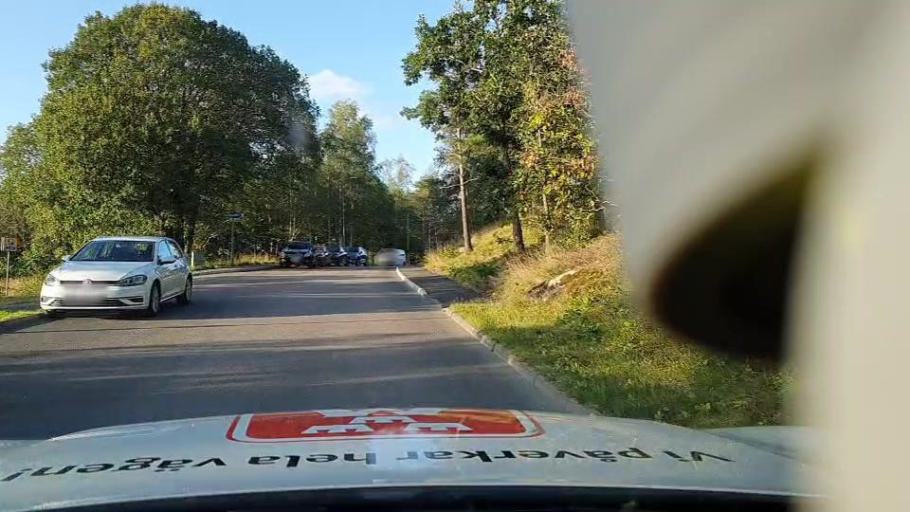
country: SE
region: Vaestra Goetaland
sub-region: Goteborg
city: Loevgaerdet
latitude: 57.8124
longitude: 12.0513
